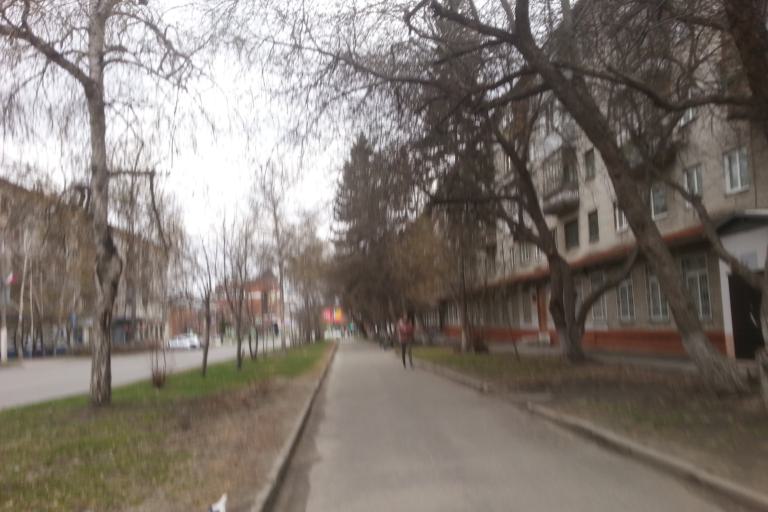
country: RU
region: Altai Krai
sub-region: Gorod Barnaulskiy
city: Barnaul
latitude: 53.3520
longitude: 83.7807
